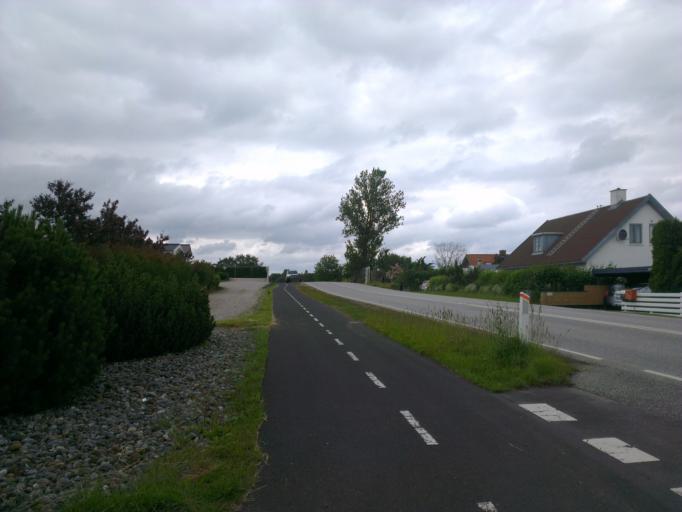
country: DK
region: Capital Region
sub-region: Frederikssund Kommune
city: Skibby
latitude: 55.6829
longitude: 11.9457
